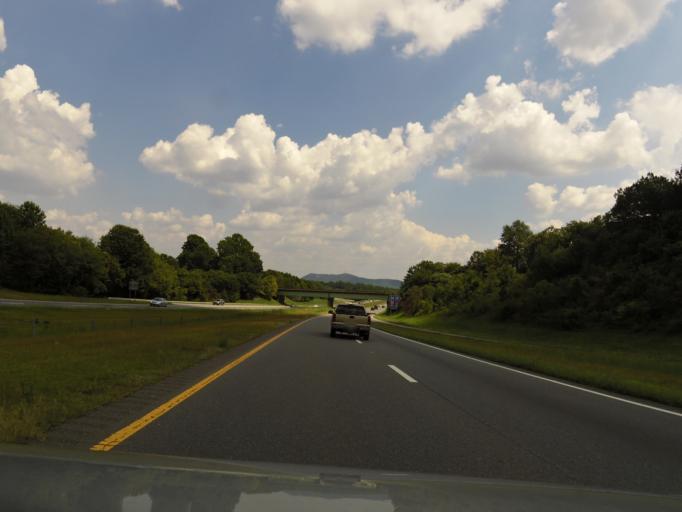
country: US
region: North Carolina
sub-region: Cleveland County
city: Kings Mountain
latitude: 35.2503
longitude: -81.3382
